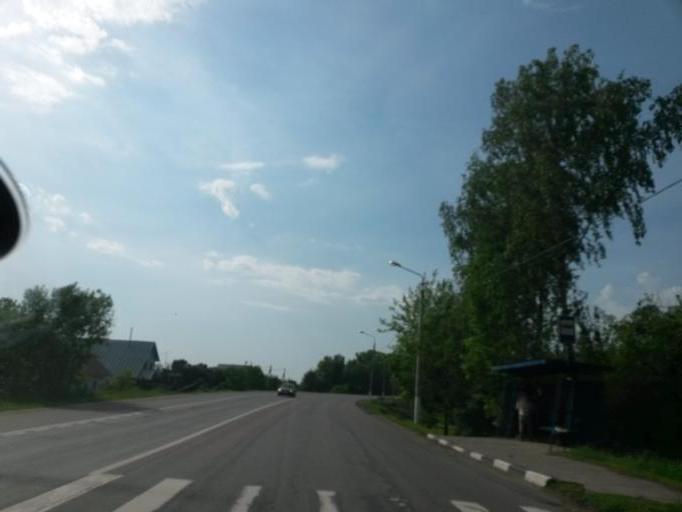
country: RU
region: Moskovskaya
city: Stolbovaya
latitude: 55.2160
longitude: 37.5050
